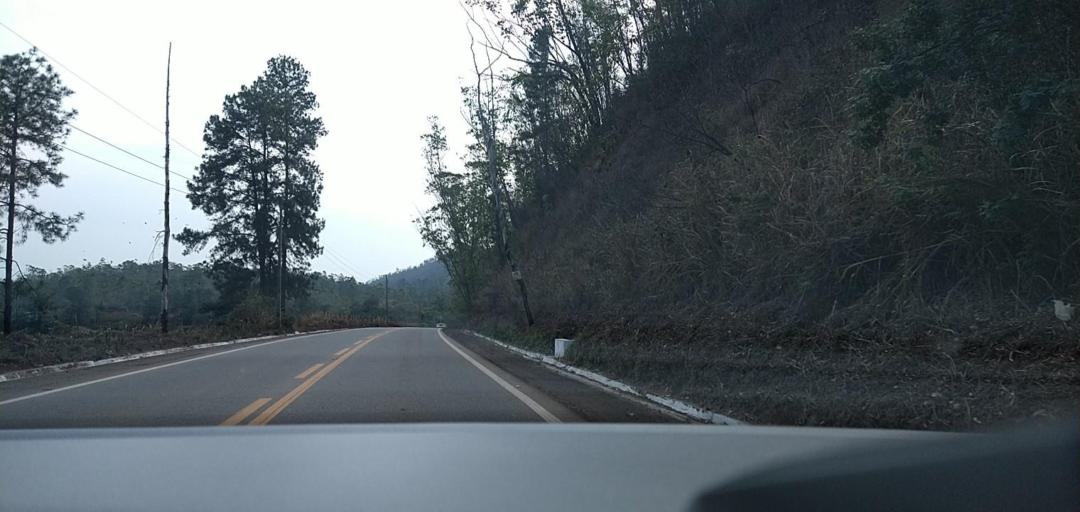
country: BR
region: Minas Gerais
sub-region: Rio Piracicaba
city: Rio Piracicaba
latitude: -19.8782
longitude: -43.1254
